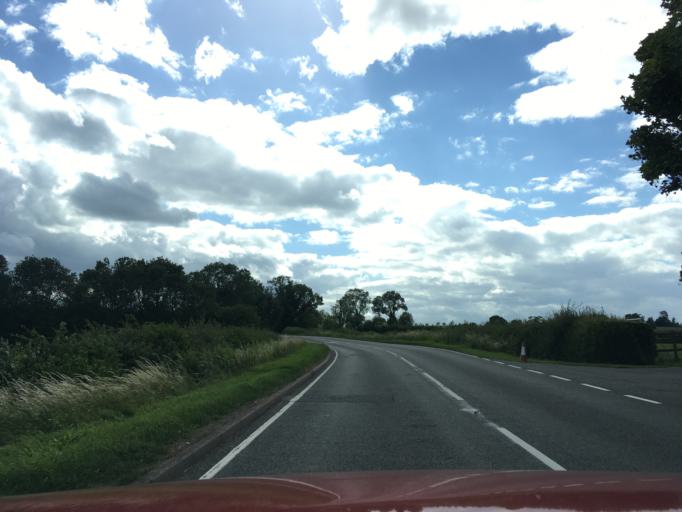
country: GB
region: England
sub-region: Leicestershire
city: Coalville
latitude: 52.7740
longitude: -1.3688
